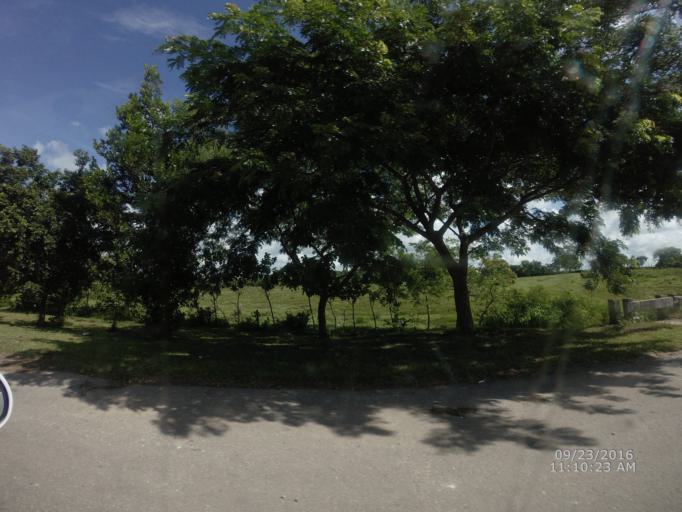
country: CU
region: La Habana
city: Arroyo Naranjo
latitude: 23.0201
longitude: -82.2555
